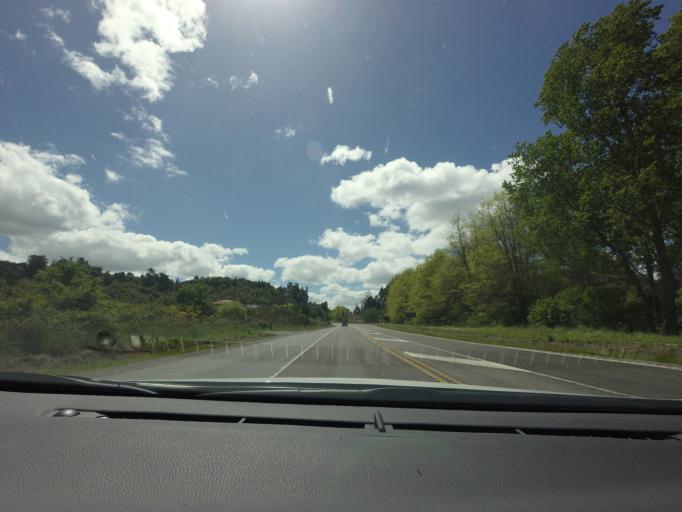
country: NZ
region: Bay of Plenty
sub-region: Rotorua District
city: Rotorua
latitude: -38.1785
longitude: 176.2490
